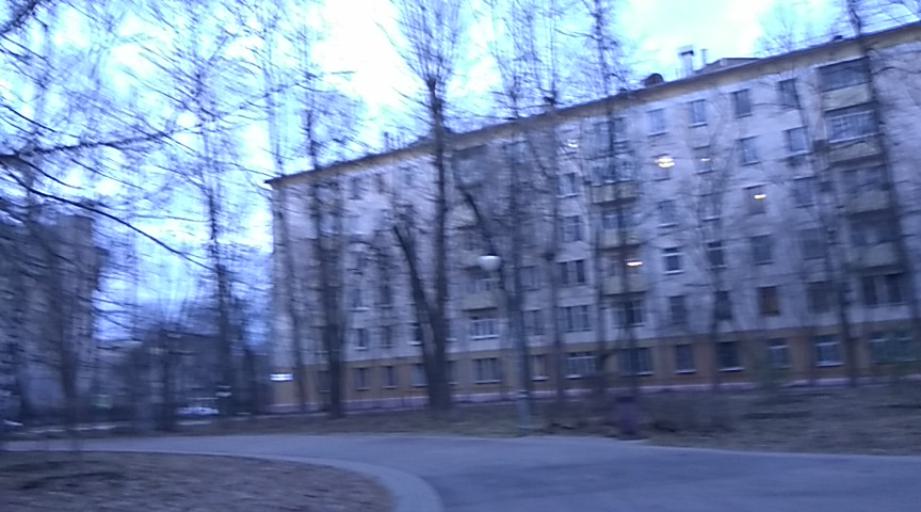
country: RU
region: Moskovskaya
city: Semenovskoye
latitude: 55.6947
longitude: 37.5449
